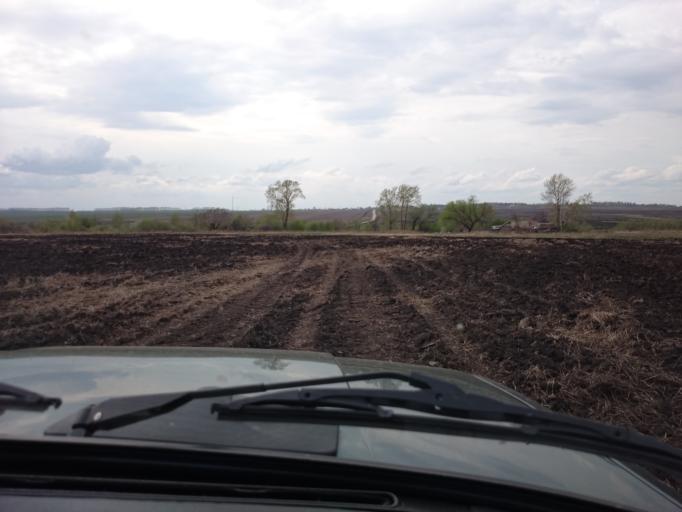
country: RU
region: Mordoviya
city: Kadoshkino
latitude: 54.0179
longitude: 44.4622
